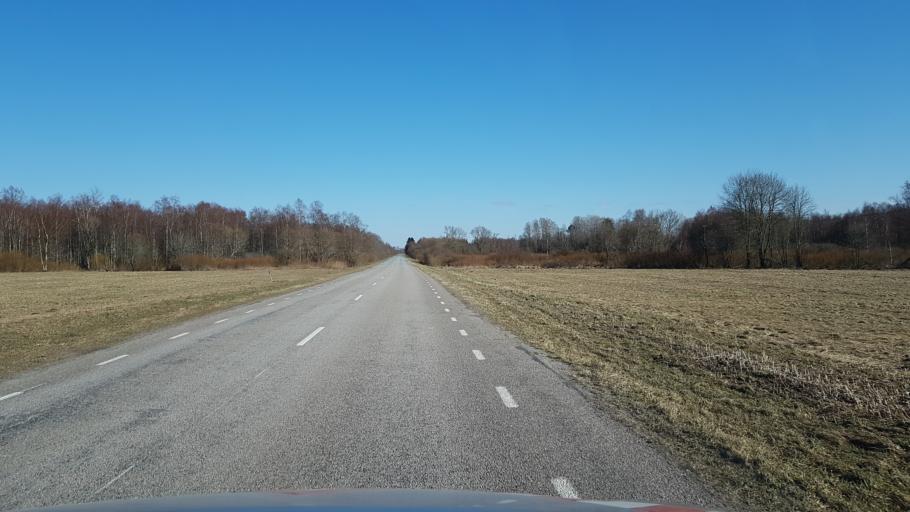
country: EE
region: Laeaene-Virumaa
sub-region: Haljala vald
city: Haljala
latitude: 59.5087
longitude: 26.1093
